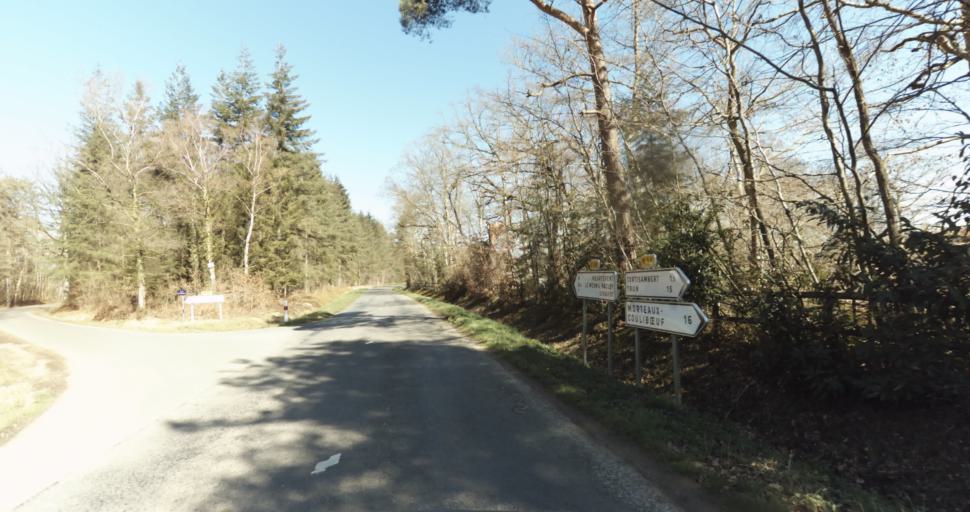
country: FR
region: Lower Normandy
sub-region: Departement du Calvados
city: Livarot
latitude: 48.9662
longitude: 0.0981
